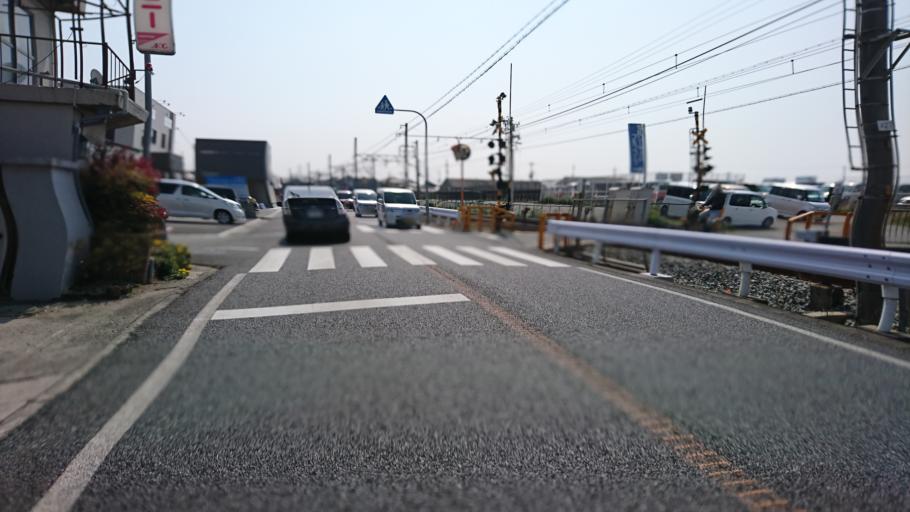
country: JP
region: Hyogo
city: Shirahamacho-usazakiminami
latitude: 34.7768
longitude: 134.7632
